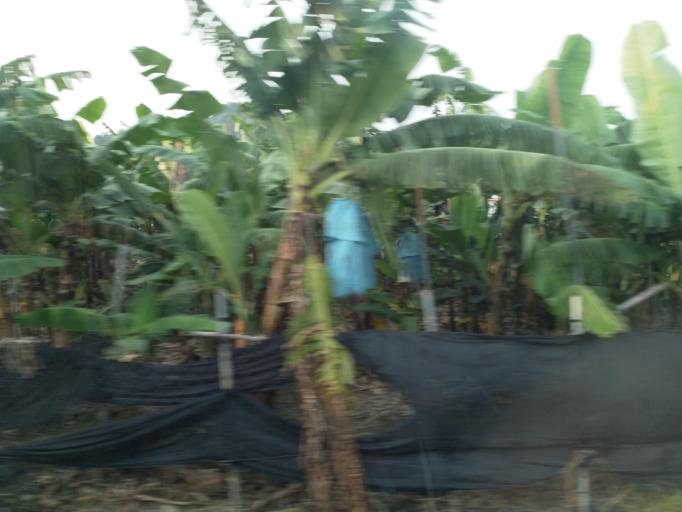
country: TW
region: Taiwan
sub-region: Pingtung
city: Pingtung
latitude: 22.8845
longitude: 120.5005
